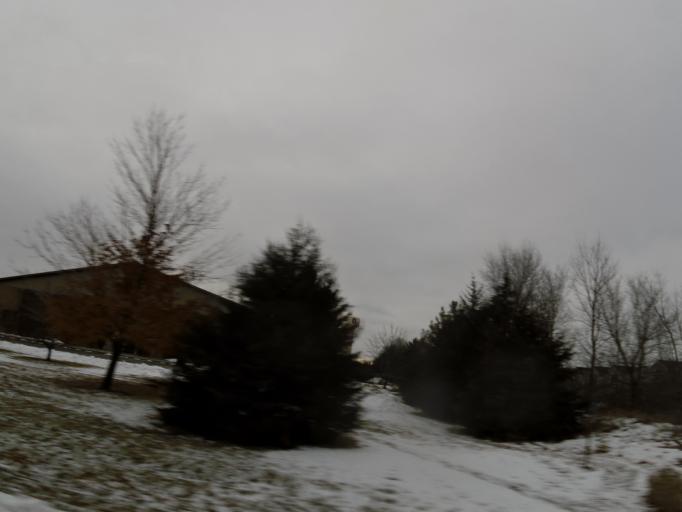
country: US
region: Minnesota
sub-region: Scott County
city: Jordan
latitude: 44.6815
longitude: -93.6398
